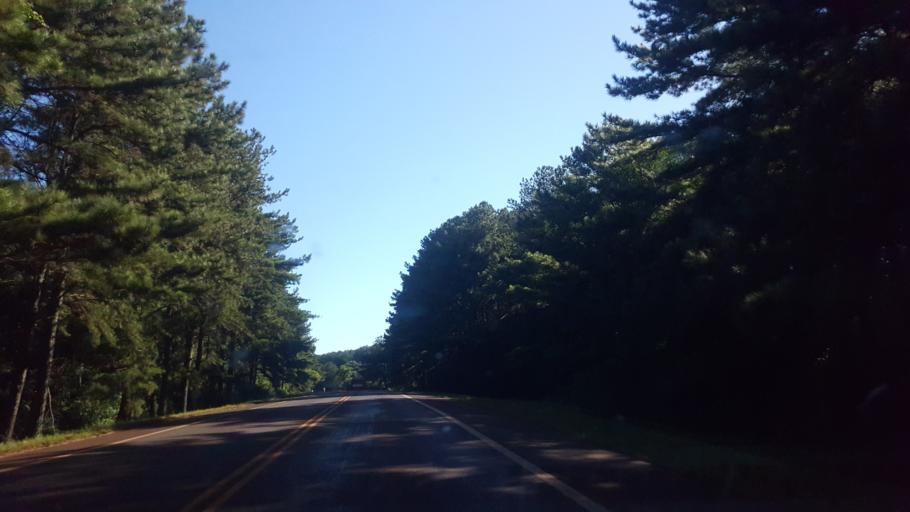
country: AR
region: Misiones
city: Puerto Libertad
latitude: -25.9056
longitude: -54.5658
